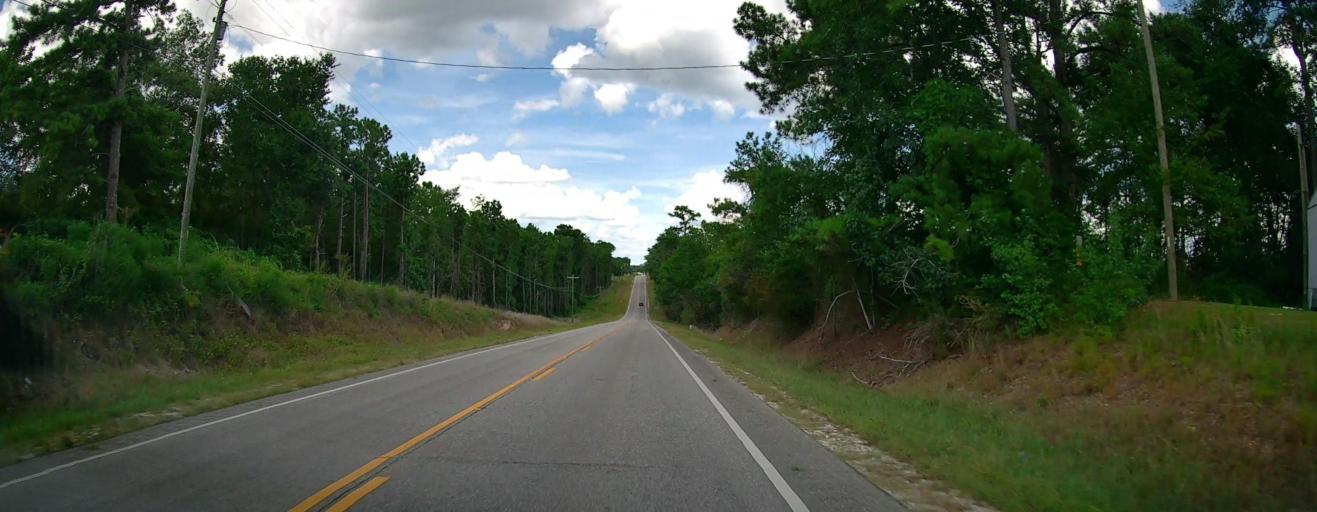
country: US
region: Alabama
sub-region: Macon County
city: Tuskegee
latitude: 32.4657
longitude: -85.5919
